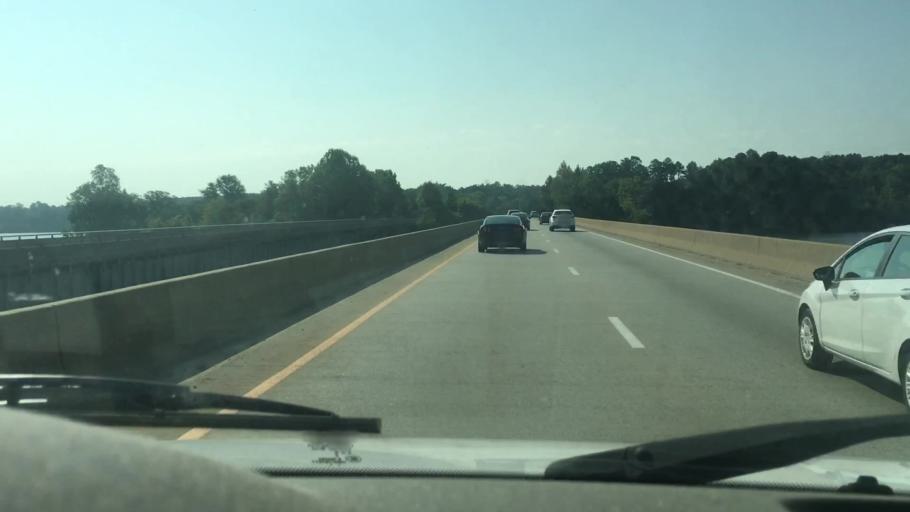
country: US
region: North Carolina
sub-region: Gaston County
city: Mount Holly
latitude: 35.3502
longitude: -80.9726
